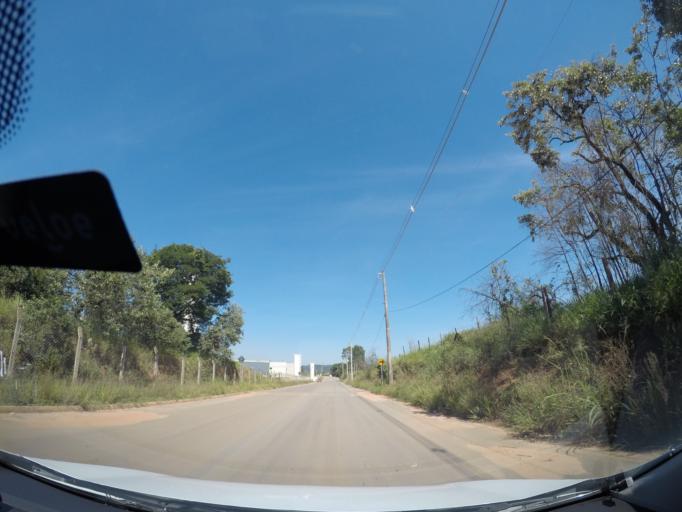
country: BR
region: Sao Paulo
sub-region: Itupeva
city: Itupeva
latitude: -23.1259
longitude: -47.0184
